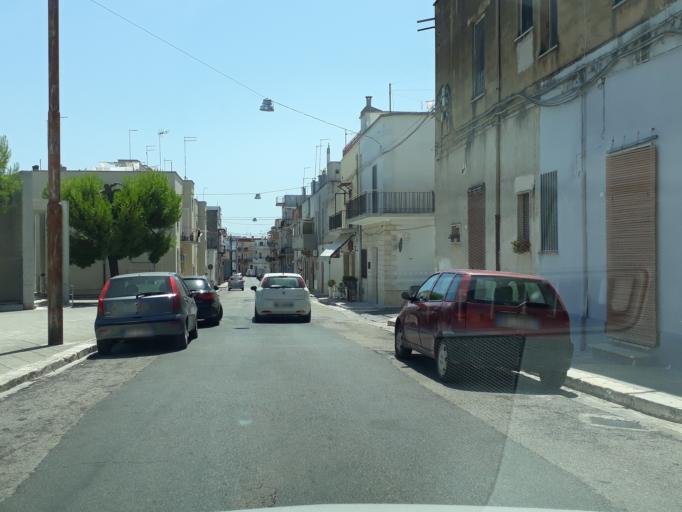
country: IT
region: Apulia
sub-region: Provincia di Brindisi
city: Carovigno
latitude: 40.7042
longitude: 17.6610
